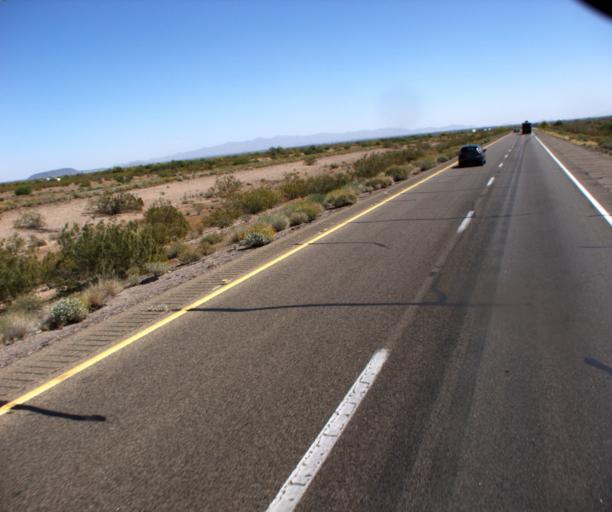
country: US
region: Arizona
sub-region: Maricopa County
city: Buckeye
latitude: 33.5034
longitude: -112.9700
